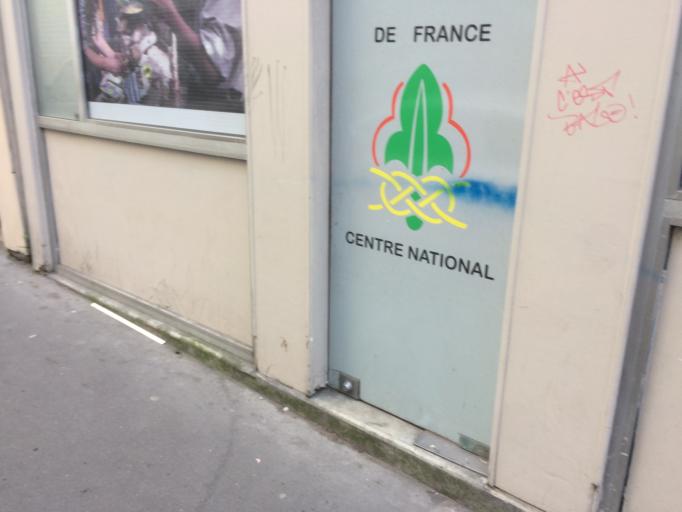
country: FR
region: Ile-de-France
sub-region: Departement de Seine-Saint-Denis
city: Le Pre-Saint-Gervais
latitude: 48.8692
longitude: 2.3895
